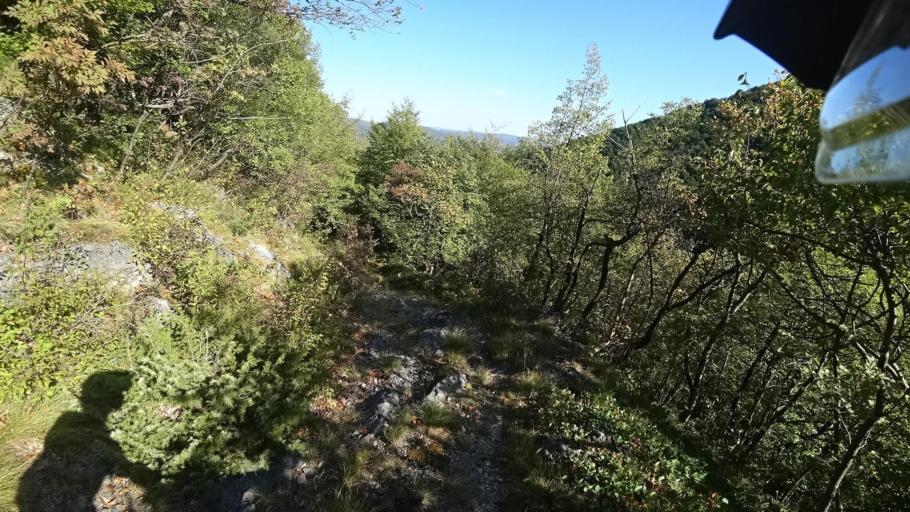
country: HR
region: Karlovacka
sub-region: Grad Ogulin
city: Ogulin
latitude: 45.2810
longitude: 15.1334
